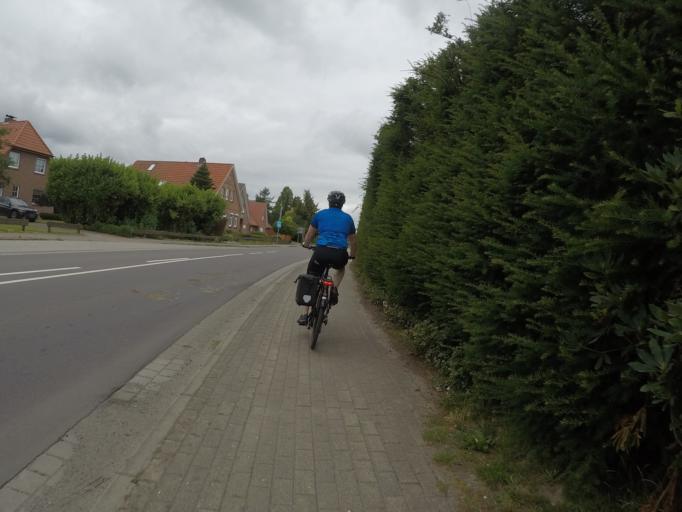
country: DE
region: Lower Saxony
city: Agathenburg
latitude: 53.5923
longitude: 9.5501
